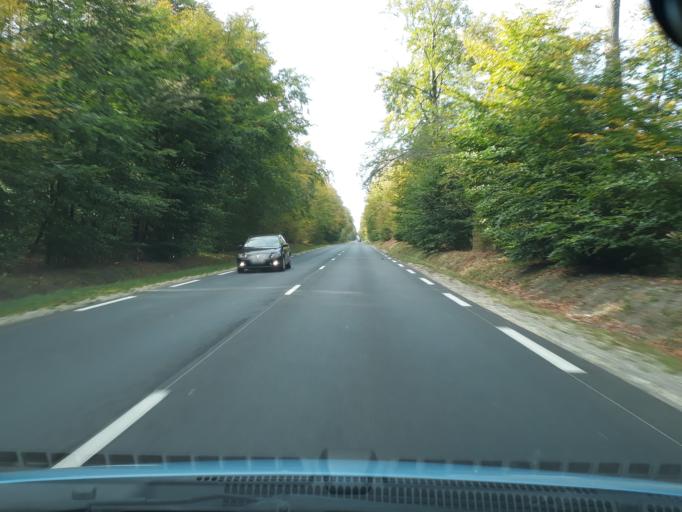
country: FR
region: Ile-de-France
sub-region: Departement de Seine-et-Marne
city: Fontainebleau
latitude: 48.3707
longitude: 2.6405
